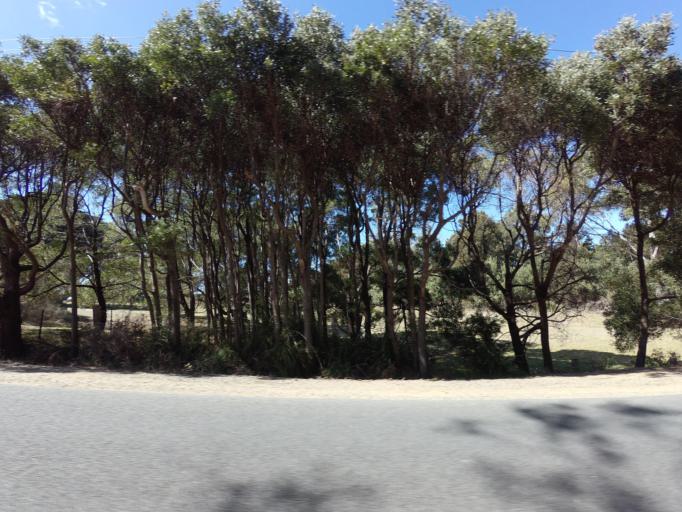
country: AU
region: Tasmania
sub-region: Break O'Day
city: St Helens
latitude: -41.6841
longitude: 148.2818
